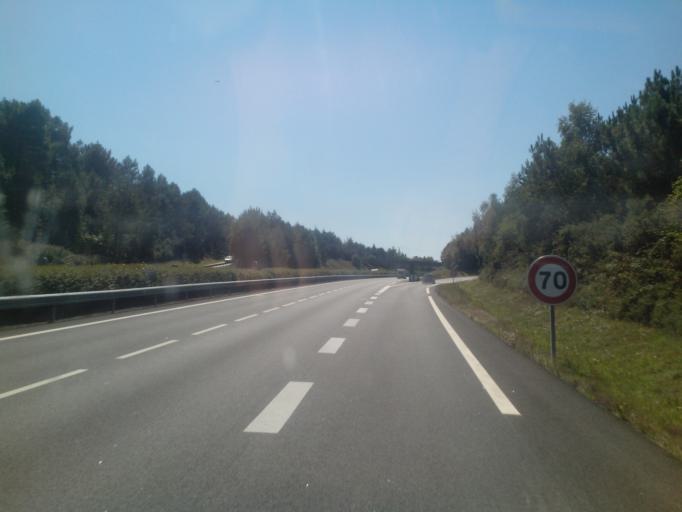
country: FR
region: Brittany
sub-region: Departement du Morbihan
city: Molac
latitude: 47.7822
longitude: -2.4579
